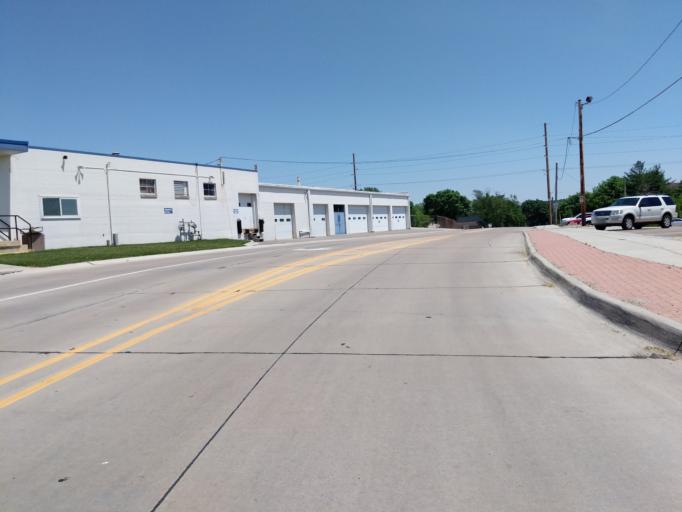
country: US
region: Iowa
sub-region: Linn County
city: Cedar Rapids
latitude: 42.0194
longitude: -91.6322
